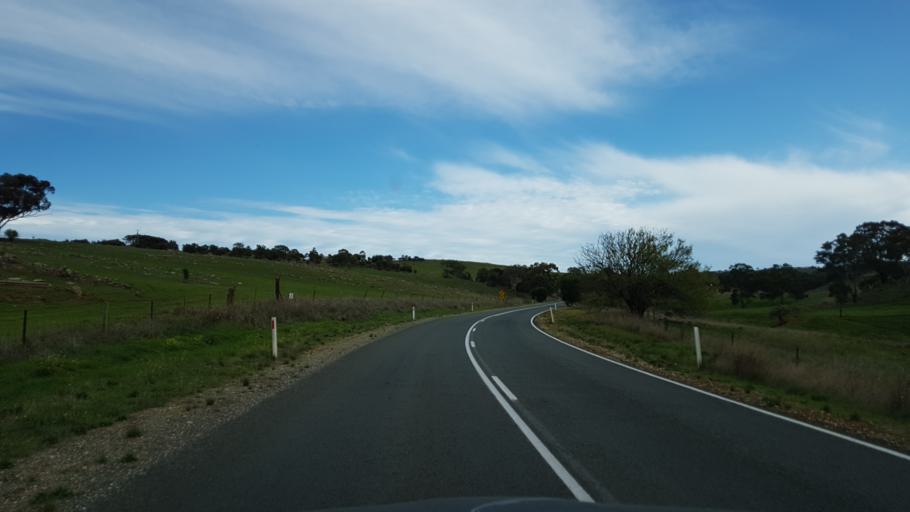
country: AU
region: South Australia
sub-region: Alexandrina
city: Strathalbyn
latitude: -35.1854
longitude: 138.9511
